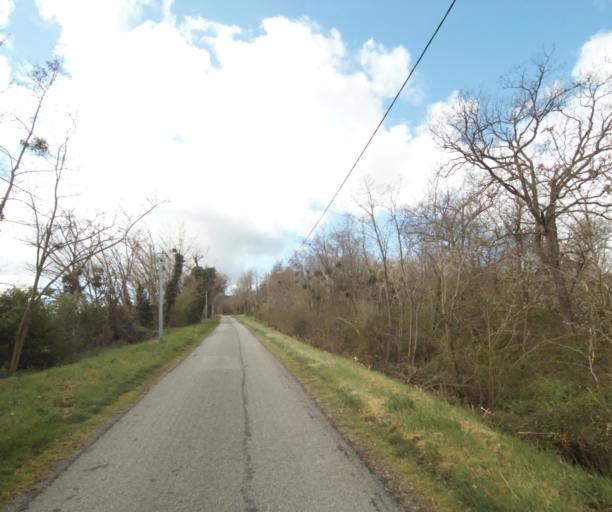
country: FR
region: Midi-Pyrenees
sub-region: Departement de l'Ariege
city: Saverdun
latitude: 43.2091
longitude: 1.5757
